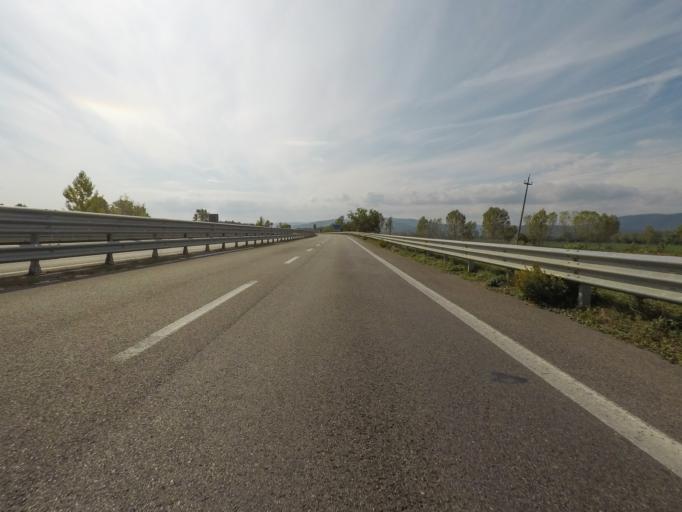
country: IT
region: Tuscany
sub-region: Provincia di Siena
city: Rosia
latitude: 43.2346
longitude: 11.2774
